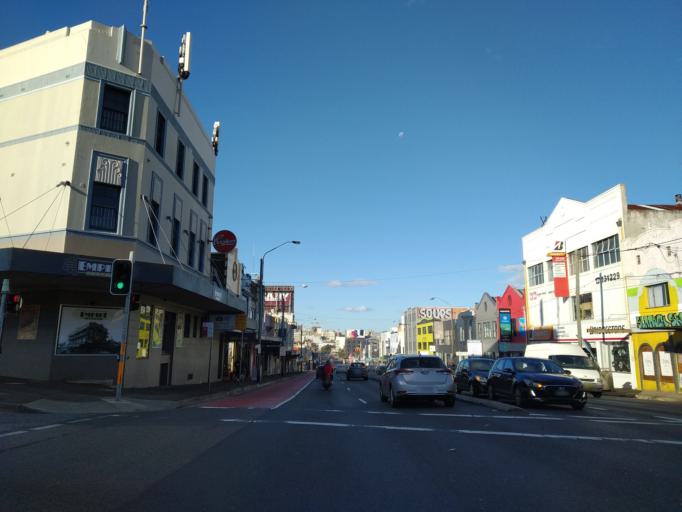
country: AU
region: New South Wales
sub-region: Marrickville
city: Camperdown
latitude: -33.8878
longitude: 151.1678
